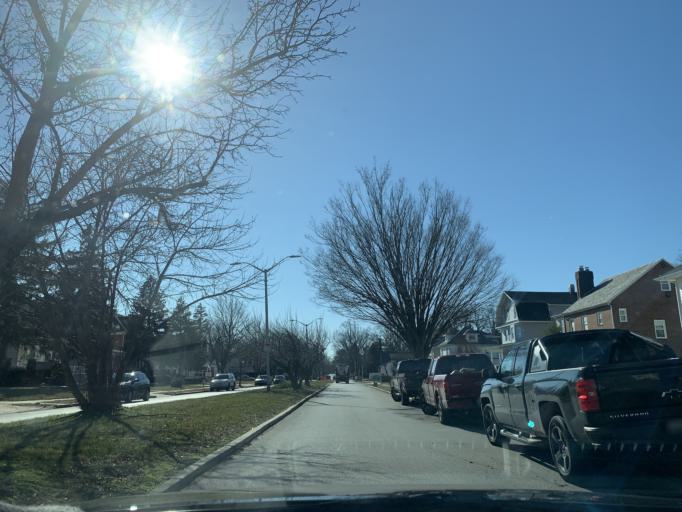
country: US
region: Maryland
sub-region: Baltimore County
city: Lochearn
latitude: 39.3281
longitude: -76.6781
